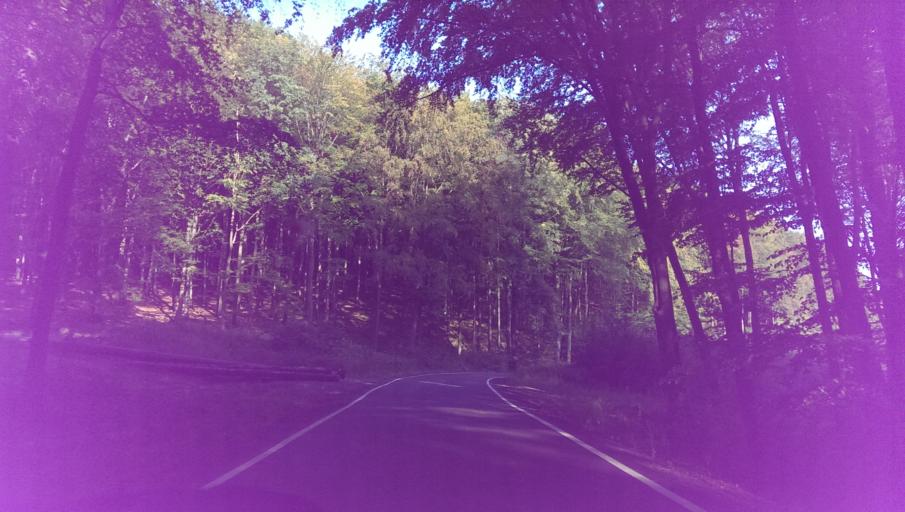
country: CZ
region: Zlin
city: Korycany
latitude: 49.0787
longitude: 17.2136
